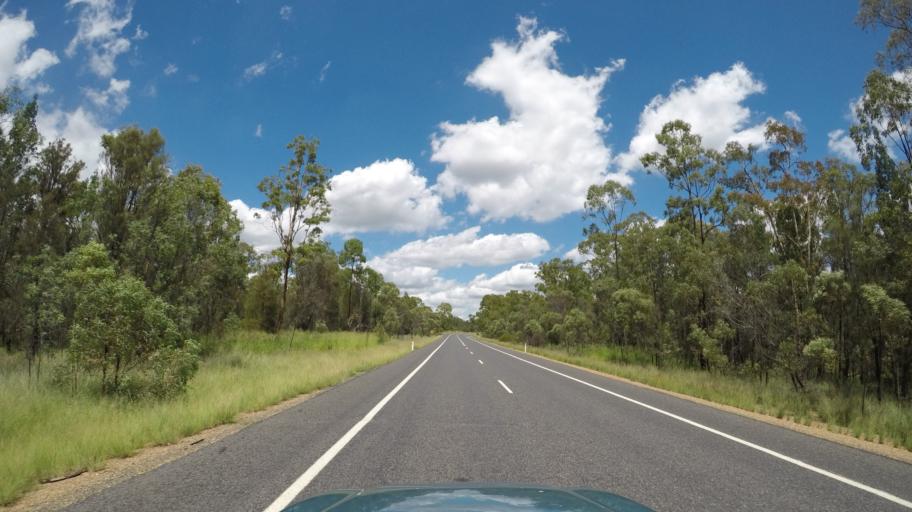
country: AU
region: Queensland
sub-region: Western Downs
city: Dalby
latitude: -27.9763
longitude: 151.0937
